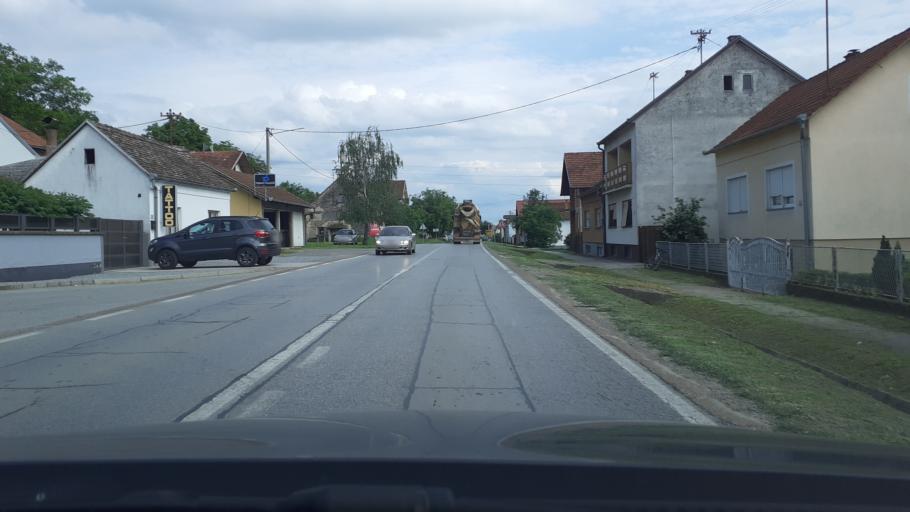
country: HR
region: Brodsko-Posavska
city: Sibinj
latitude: 45.1871
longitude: 17.9212
